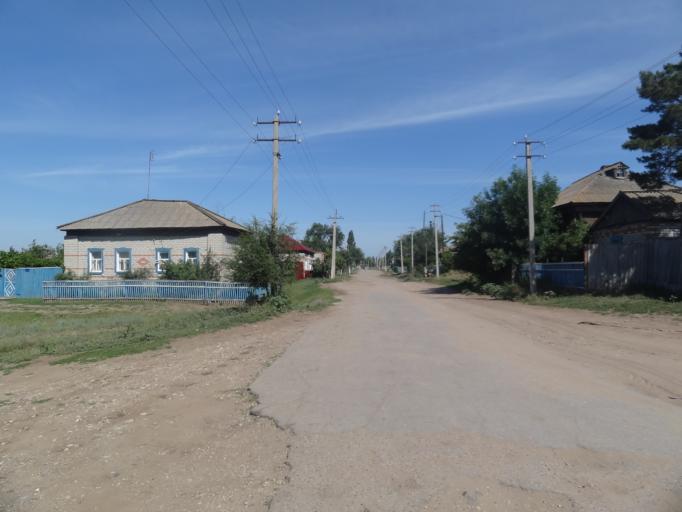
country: RU
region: Saratov
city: Krasnoarmeysk
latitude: 51.0898
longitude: 45.9510
